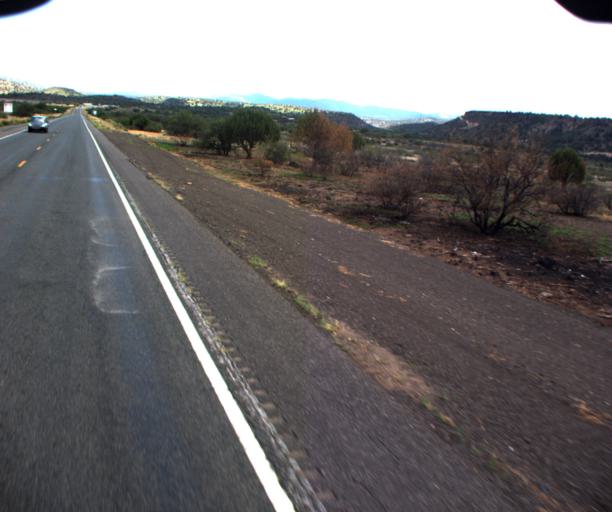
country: US
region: Arizona
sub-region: Yavapai County
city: Camp Verde
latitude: 34.5147
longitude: -112.0061
